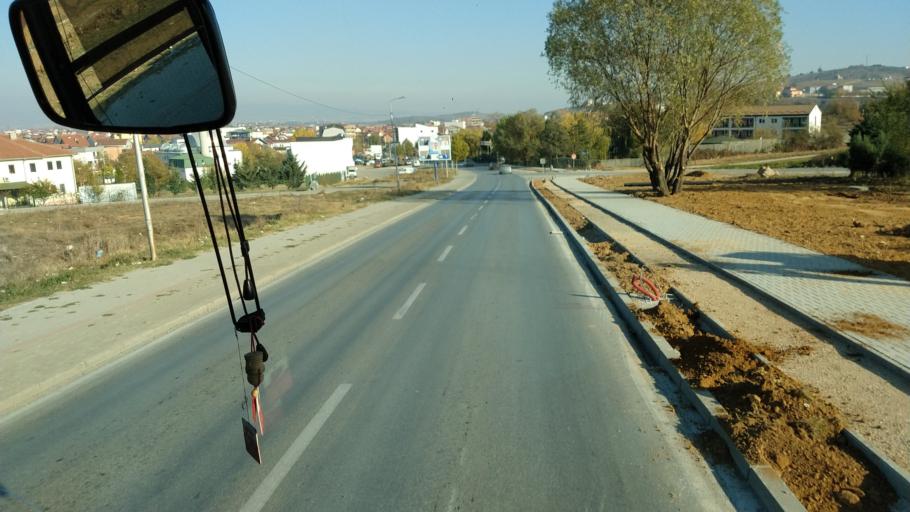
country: XK
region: Ferizaj
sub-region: Komuna e Shtimes
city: Shtime
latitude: 42.4356
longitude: 21.0268
